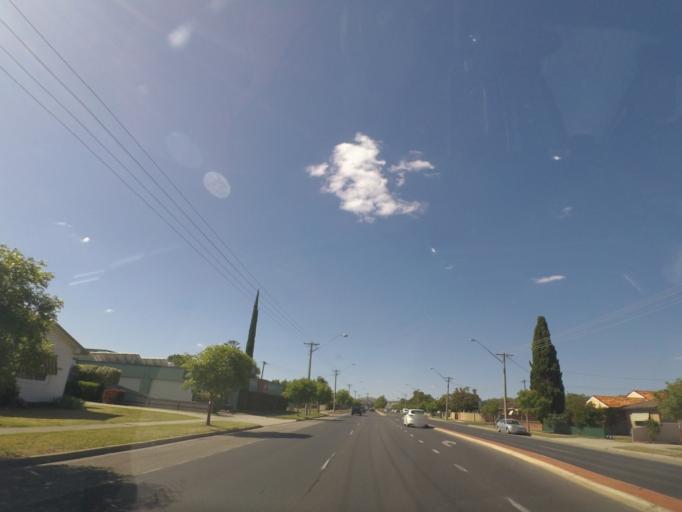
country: AU
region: New South Wales
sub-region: Albury Municipality
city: North Albury
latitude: -36.0571
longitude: 146.9327
